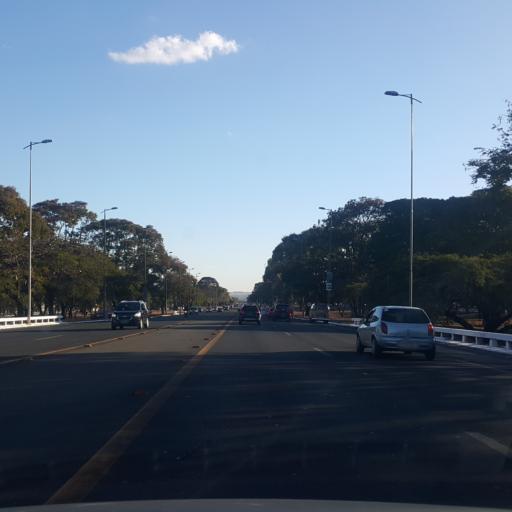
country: BR
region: Federal District
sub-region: Brasilia
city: Brasilia
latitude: -15.8240
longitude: -47.9105
